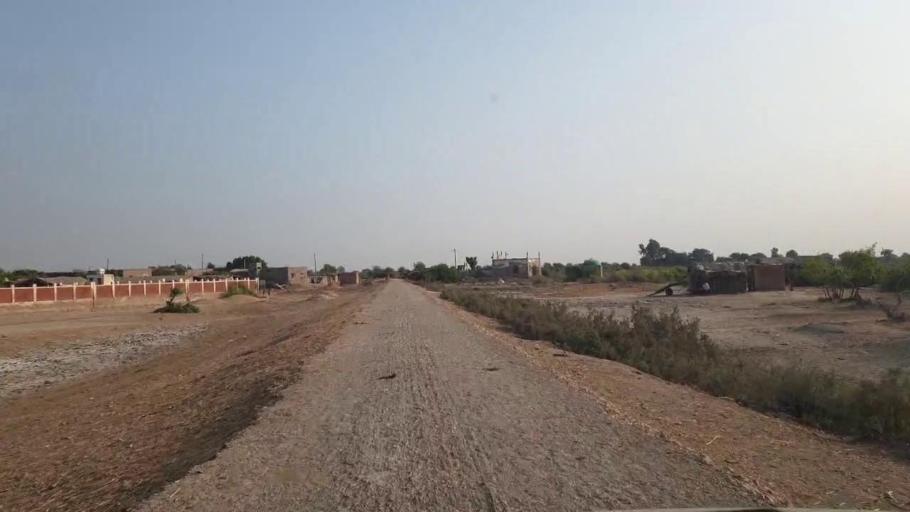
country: PK
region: Sindh
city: Rajo Khanani
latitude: 25.0190
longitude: 68.7837
